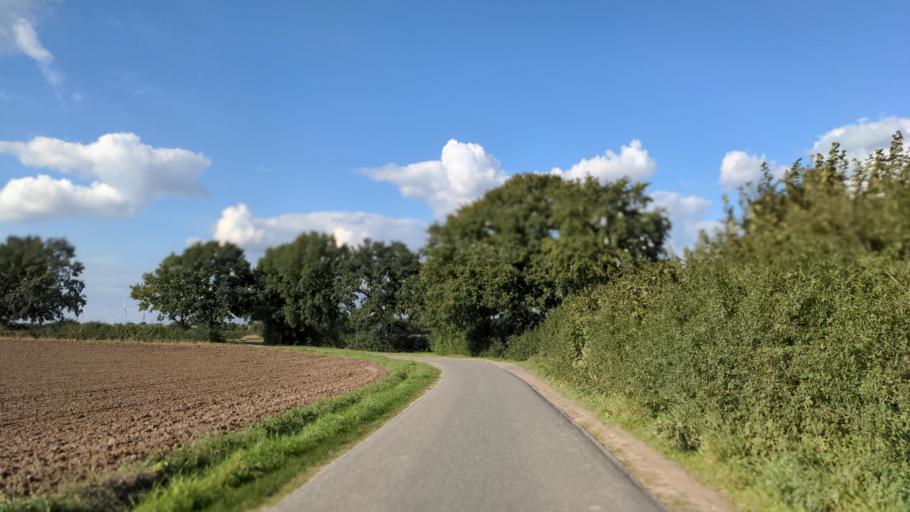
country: DE
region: Schleswig-Holstein
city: Monkhagen
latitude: 53.9032
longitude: 10.5958
